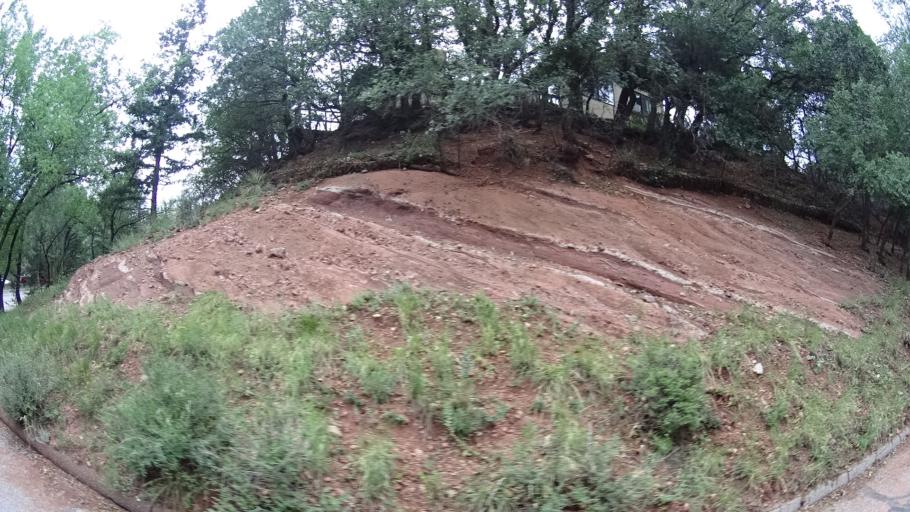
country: US
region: Colorado
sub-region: El Paso County
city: Manitou Springs
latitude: 38.8528
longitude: -104.8940
